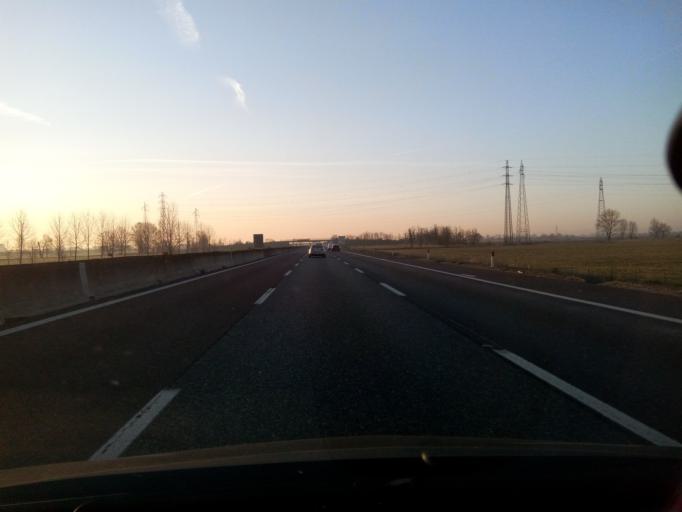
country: IT
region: Lombardy
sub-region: Citta metropolitana di Milano
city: San Giuliano Milanese
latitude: 45.3682
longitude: 9.2875
